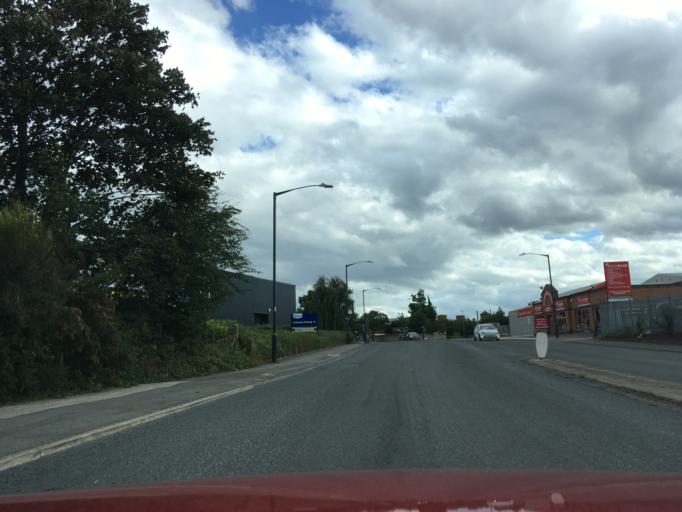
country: GB
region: England
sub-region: Warwickshire
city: Nuneaton
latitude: 52.5290
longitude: -1.4624
